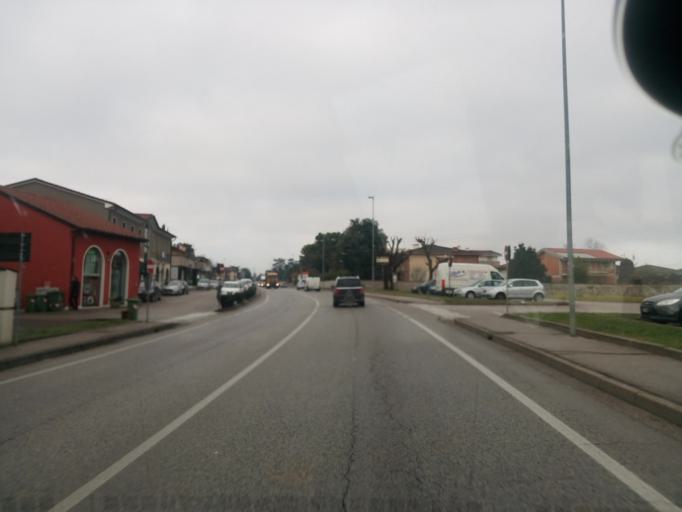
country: IT
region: Veneto
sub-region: Provincia di Vicenza
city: Sandrigo
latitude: 45.6625
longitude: 11.6049
